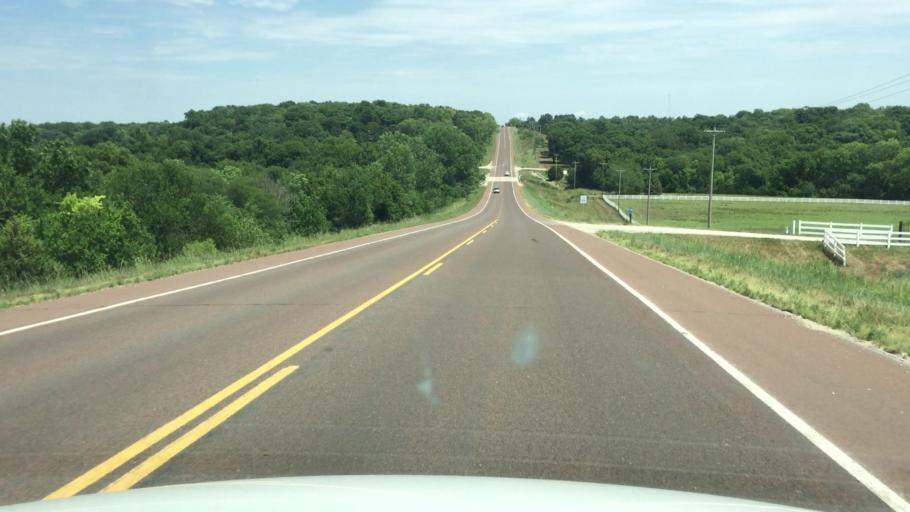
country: US
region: Kansas
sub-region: Douglas County
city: Lawrence
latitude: 38.9713
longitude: -95.3963
